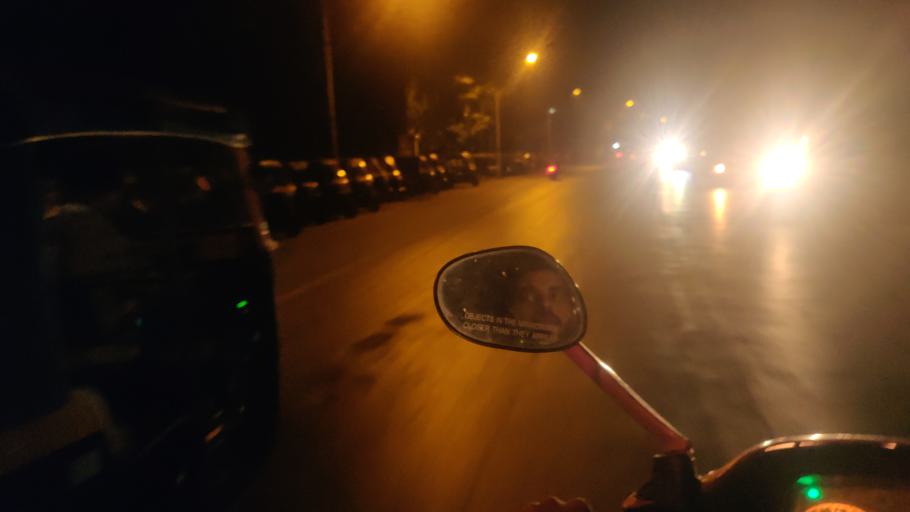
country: IN
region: Maharashtra
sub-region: Thane
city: Bhayandar
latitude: 19.2992
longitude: 72.8344
